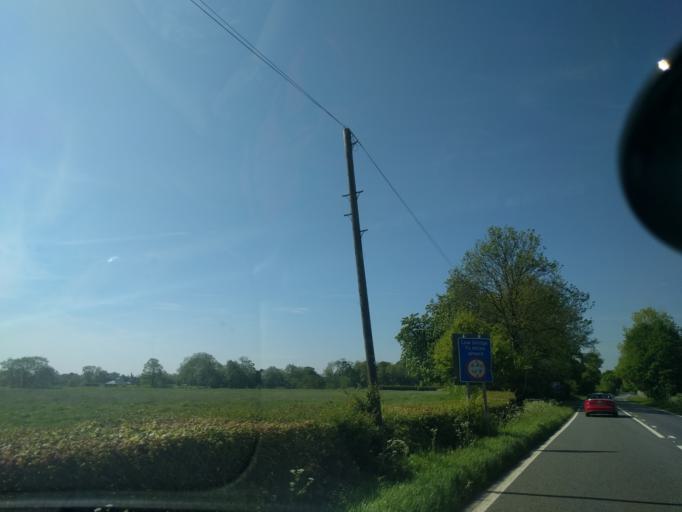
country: GB
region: England
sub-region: Somerset
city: Castle Cary
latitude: 51.0847
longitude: -2.6116
